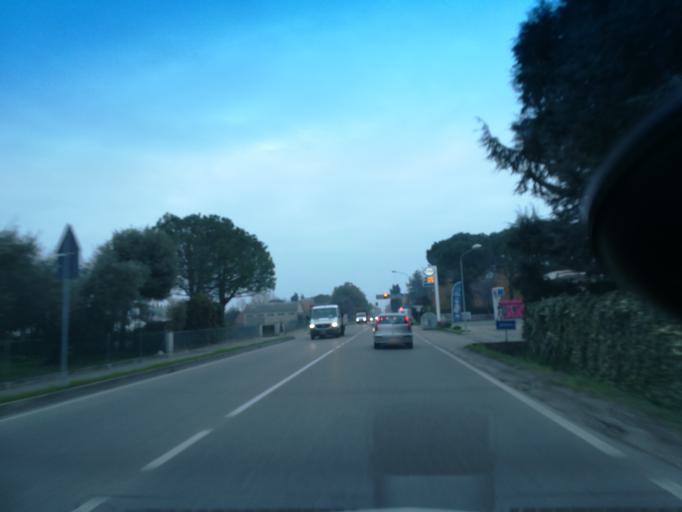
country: IT
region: Emilia-Romagna
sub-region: Provincia di Ravenna
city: Castel Bolognese
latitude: 44.3234
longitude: 11.7903
